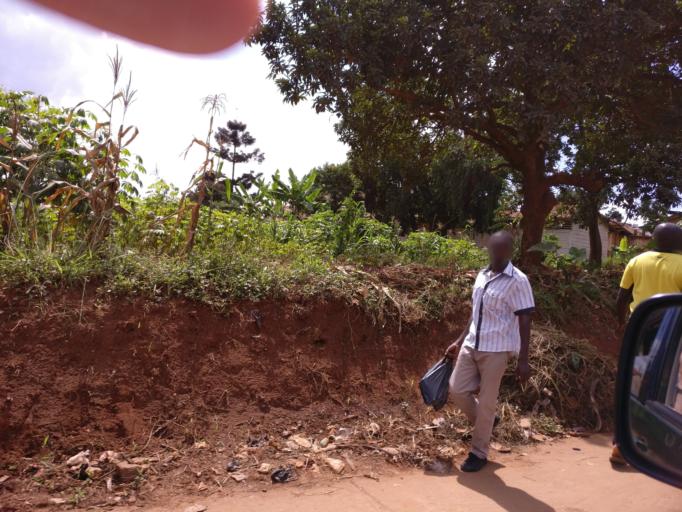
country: UG
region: Central Region
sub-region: Kampala District
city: Kampala
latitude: 0.2798
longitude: 32.5644
